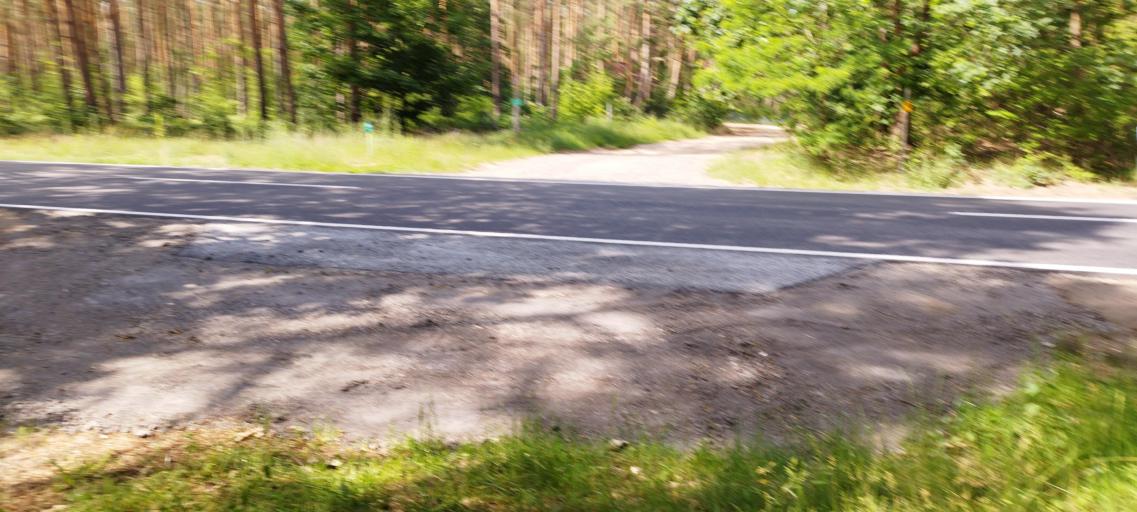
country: DE
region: Brandenburg
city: Rauen
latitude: 52.3592
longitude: 14.0303
